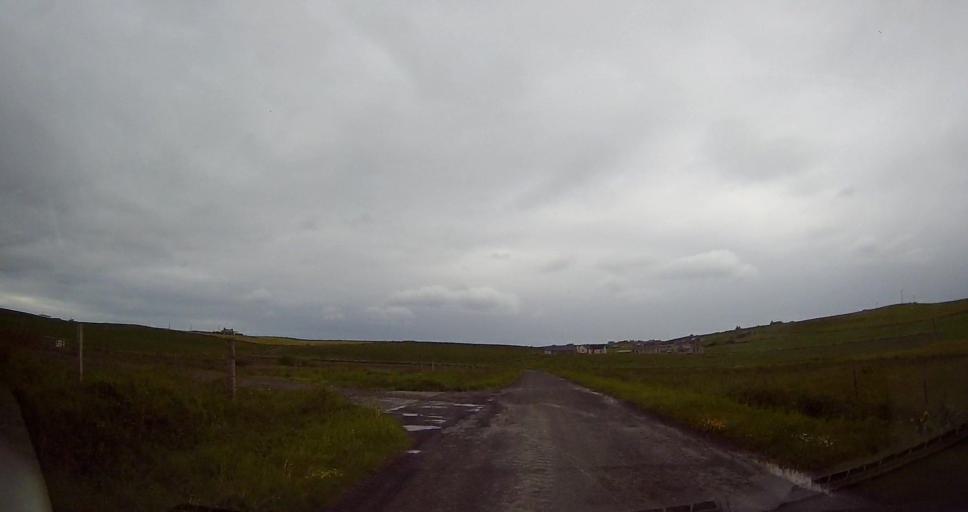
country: GB
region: Scotland
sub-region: Orkney Islands
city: Stromness
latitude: 59.0698
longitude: -3.2990
